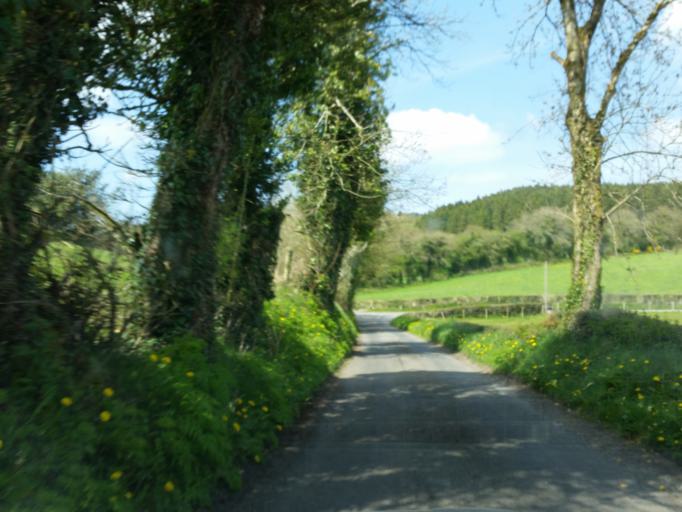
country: IE
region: Ulster
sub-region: County Monaghan
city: Clones
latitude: 54.2313
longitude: -7.3143
